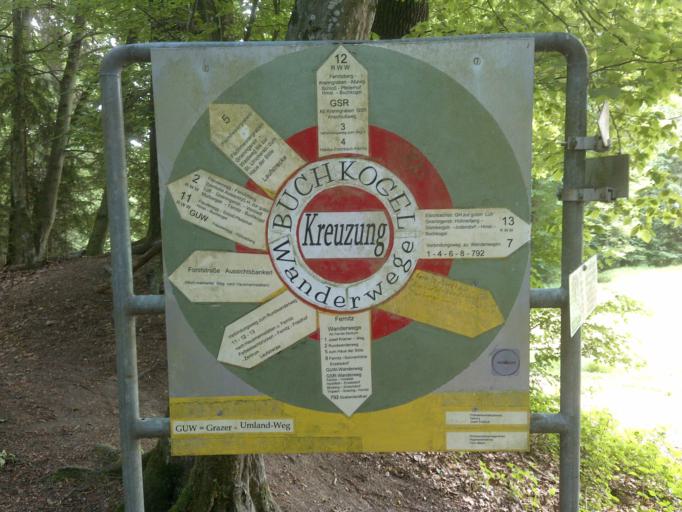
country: AT
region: Styria
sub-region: Politischer Bezirk Graz-Umgebung
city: Fernitz
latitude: 46.9746
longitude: 15.5139
